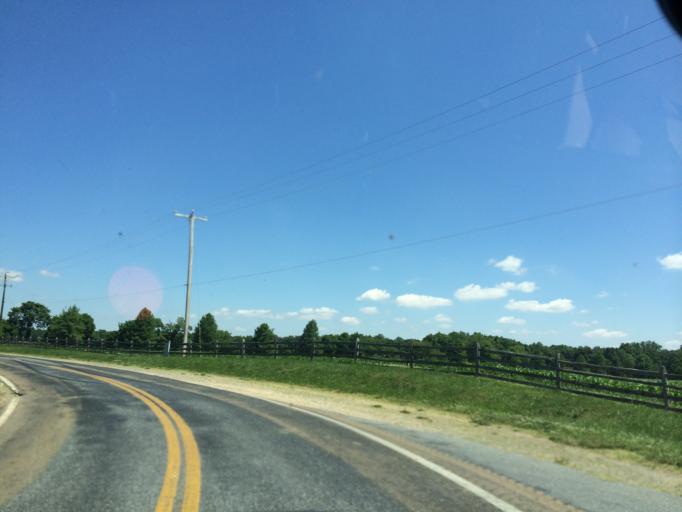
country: US
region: Maryland
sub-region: Queen Anne's County
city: Grasonville
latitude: 38.9148
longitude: -76.1246
